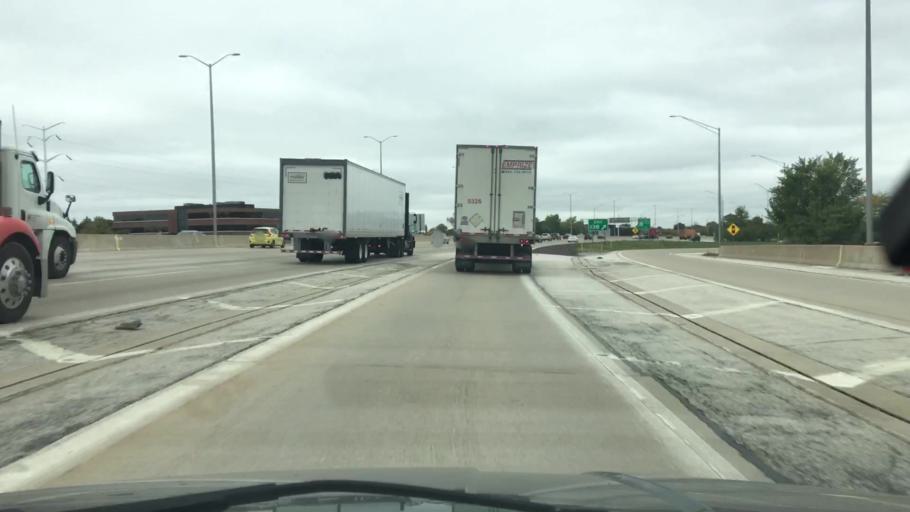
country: US
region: Illinois
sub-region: DuPage County
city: Oakbrook Terrace
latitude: 41.8459
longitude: -87.9455
